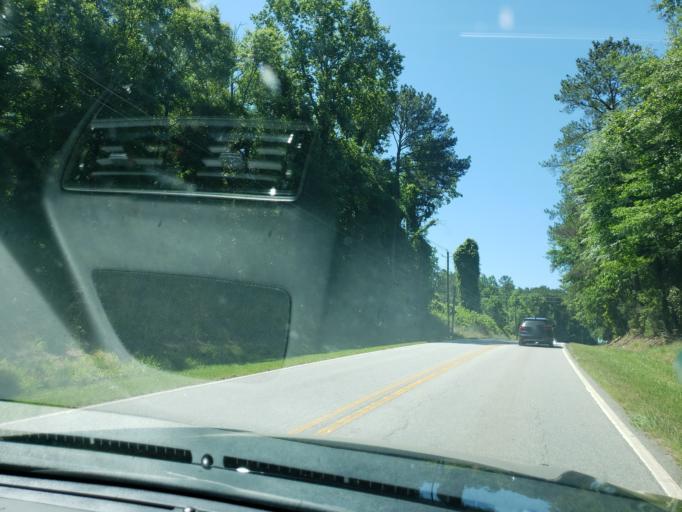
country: US
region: Alabama
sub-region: Lee County
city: Auburn
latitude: 32.6443
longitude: -85.4814
